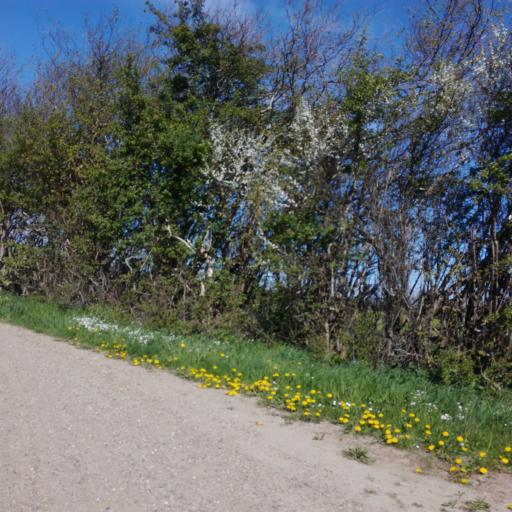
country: DK
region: South Denmark
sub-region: Vejle Kommune
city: Borkop
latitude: 55.6143
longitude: 9.6853
